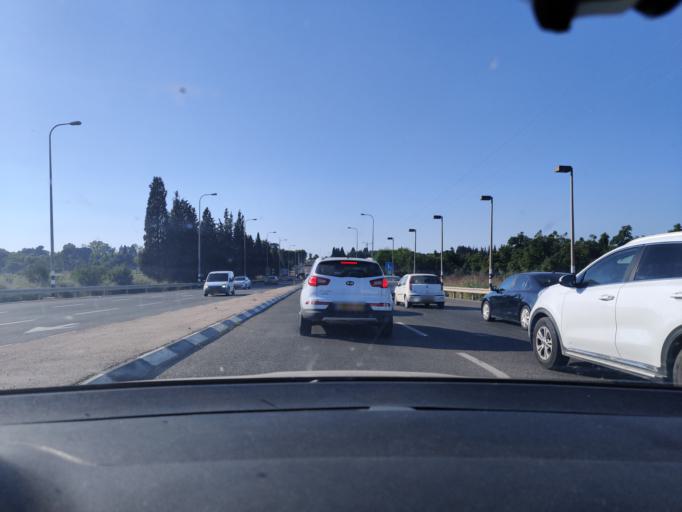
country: PS
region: West Bank
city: Nazlat `Isa
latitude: 32.4443
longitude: 35.0219
